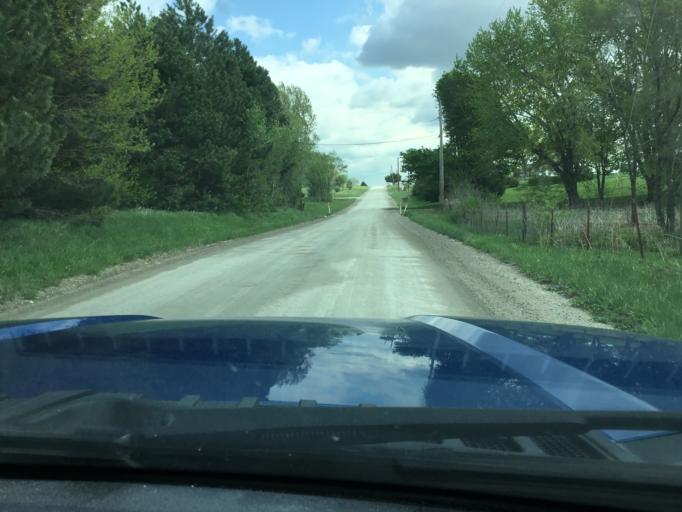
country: US
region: Kansas
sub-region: Douglas County
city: Eudora
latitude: 38.9132
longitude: -95.1112
